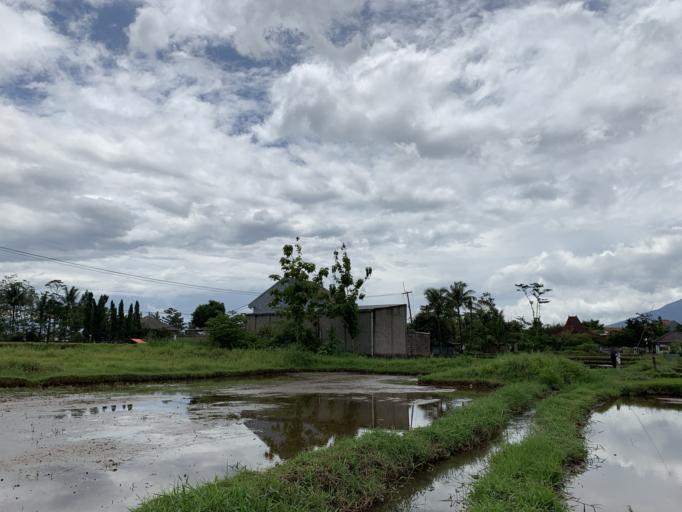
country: ID
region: West Java
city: Ciampea
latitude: -6.5663
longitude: 106.7453
